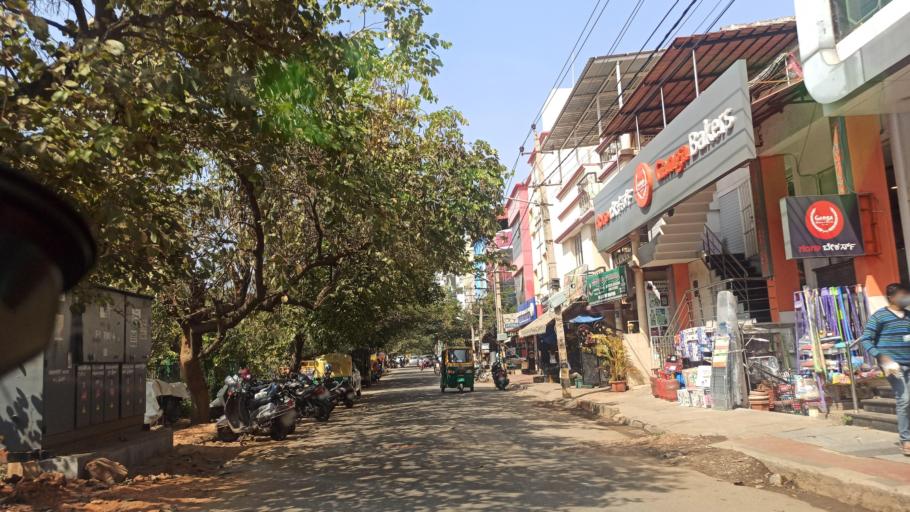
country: IN
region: Karnataka
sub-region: Bangalore Urban
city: Yelahanka
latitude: 13.0627
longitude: 77.5866
